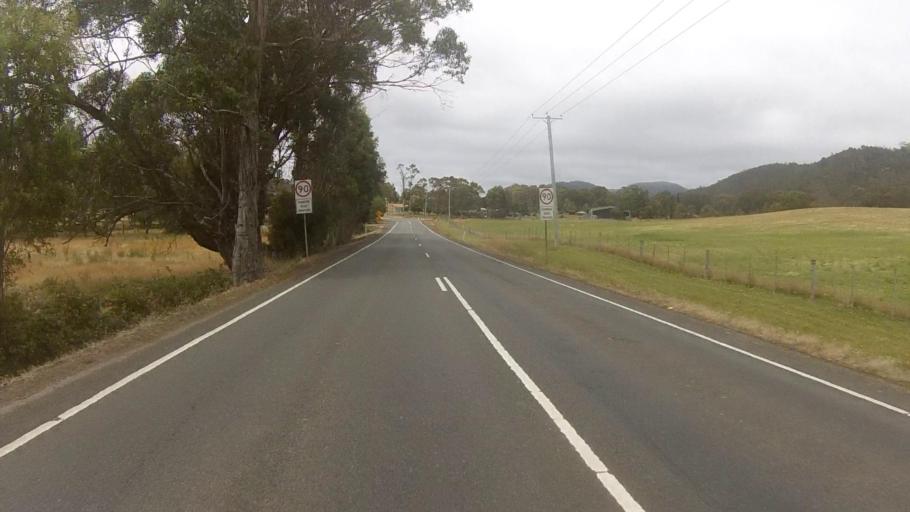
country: AU
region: Tasmania
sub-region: Kingborough
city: Margate
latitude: -42.9895
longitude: 147.1977
